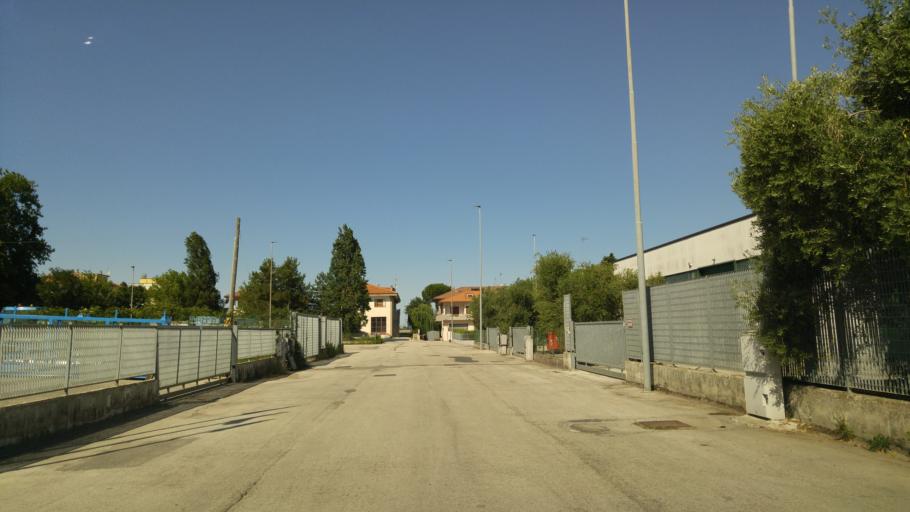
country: IT
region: The Marches
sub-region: Provincia di Pesaro e Urbino
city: Mondolfo
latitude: 43.7397
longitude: 13.1053
